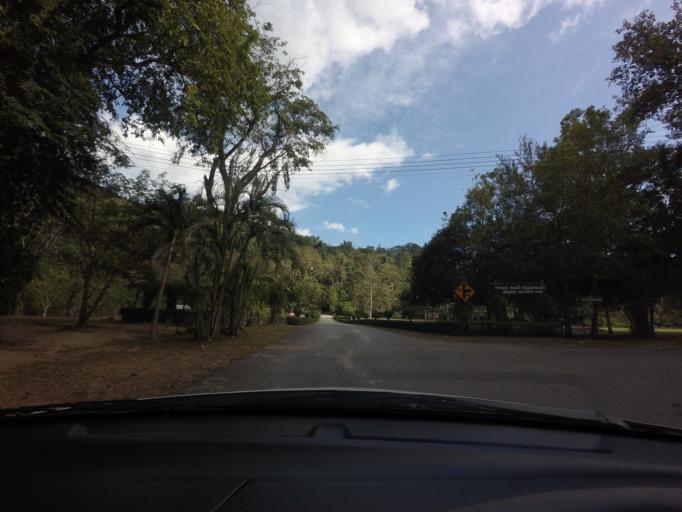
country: TH
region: Nakhon Nayok
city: Nakhon Nayok
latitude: 14.3317
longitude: 101.3055
